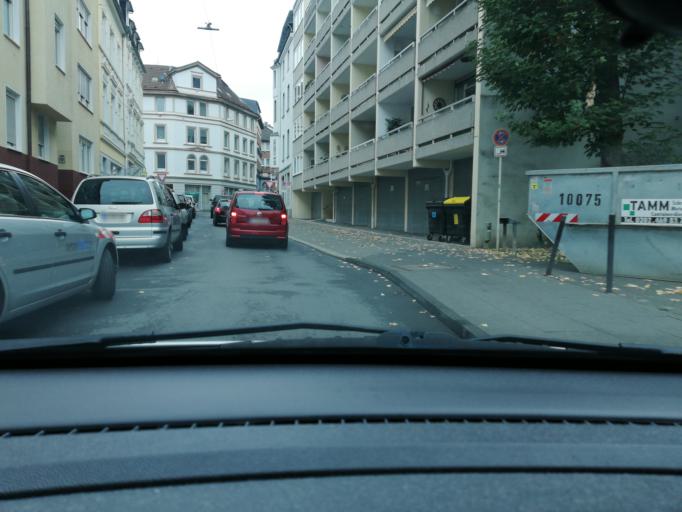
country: DE
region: North Rhine-Westphalia
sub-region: Regierungsbezirk Dusseldorf
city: Wuppertal
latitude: 51.2734
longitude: 7.2034
